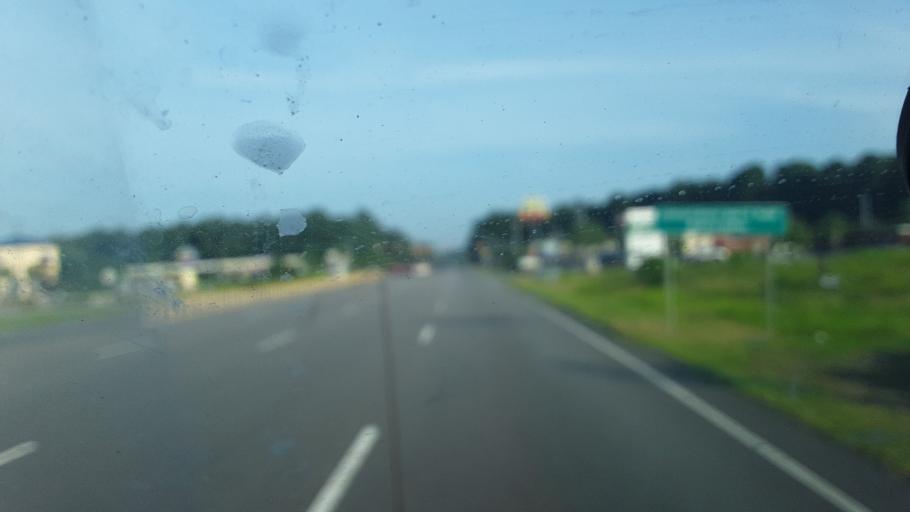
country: US
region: South Carolina
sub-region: Horry County
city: Myrtle Beach
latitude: 33.7592
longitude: -78.8577
